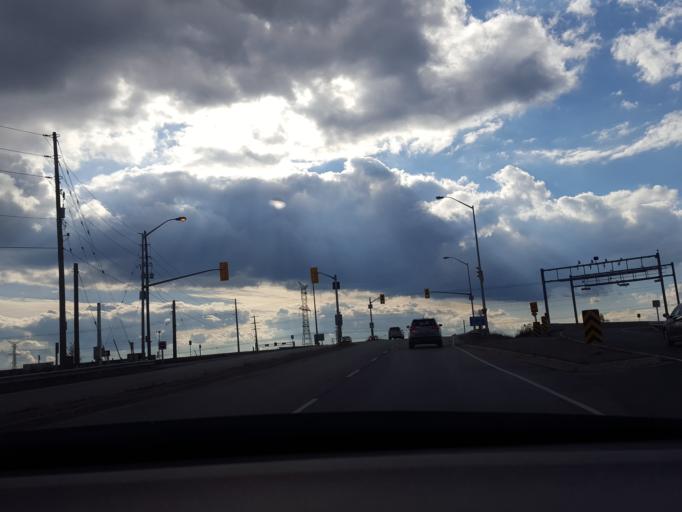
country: CA
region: Ontario
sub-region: Halton
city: Milton
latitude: 43.5732
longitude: -79.7882
